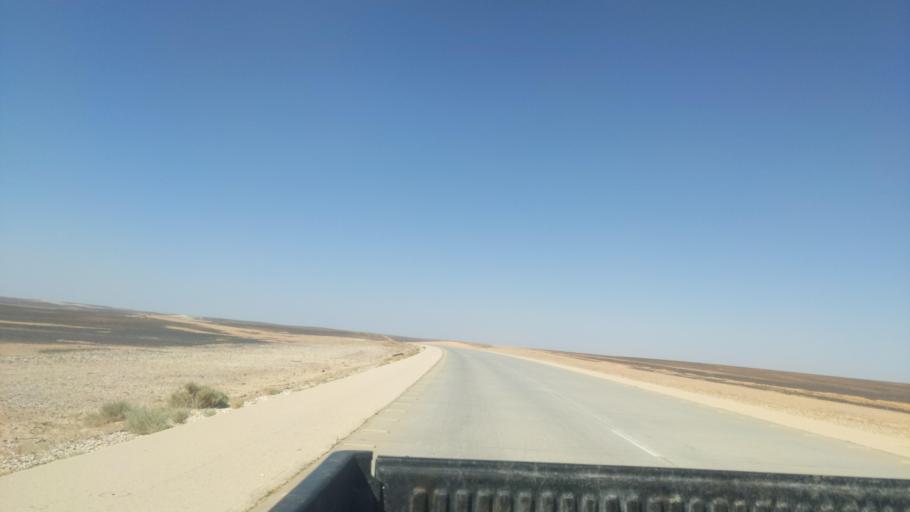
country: JO
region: Amman
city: Al Azraq ash Shamali
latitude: 31.4269
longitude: 36.7304
